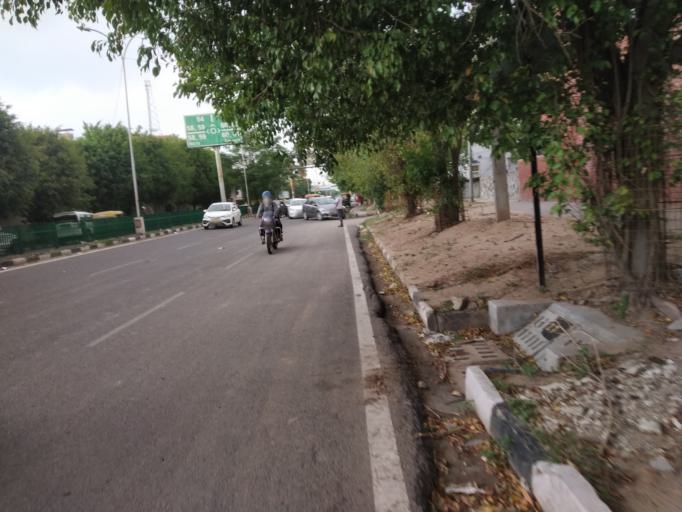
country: IN
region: Punjab
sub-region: Ajitgarh
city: Mohali
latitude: 30.7133
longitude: 76.7173
